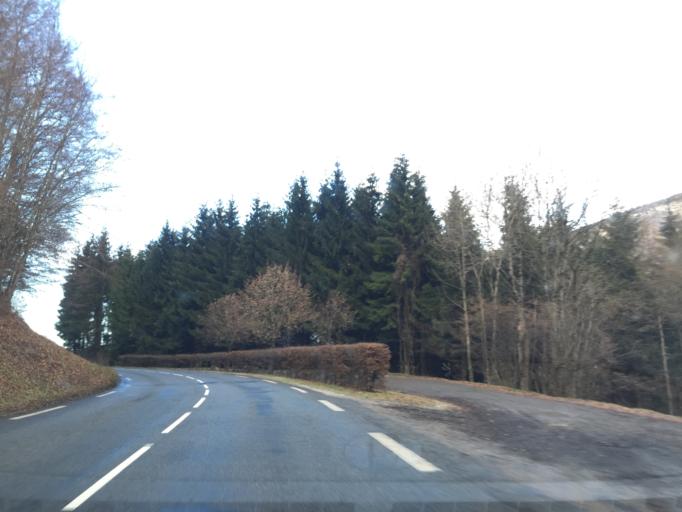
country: FR
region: Rhone-Alpes
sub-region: Departement de la Haute-Savoie
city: Gruffy
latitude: 45.7535
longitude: 6.0614
